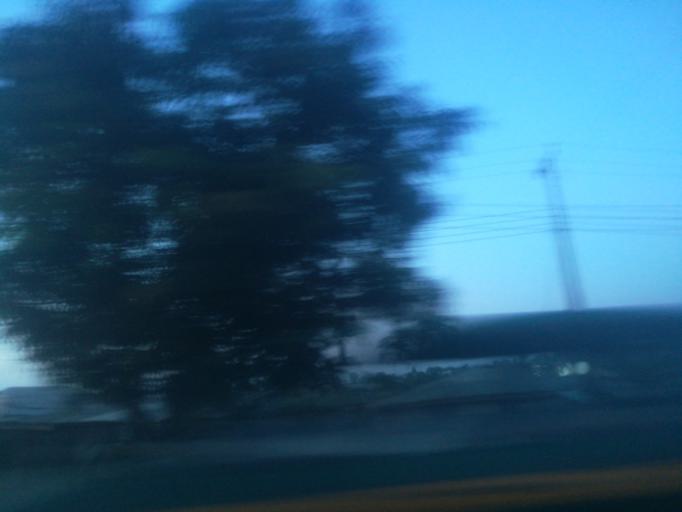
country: NG
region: Ogun
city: Abeokuta
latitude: 7.1851
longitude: 3.4291
